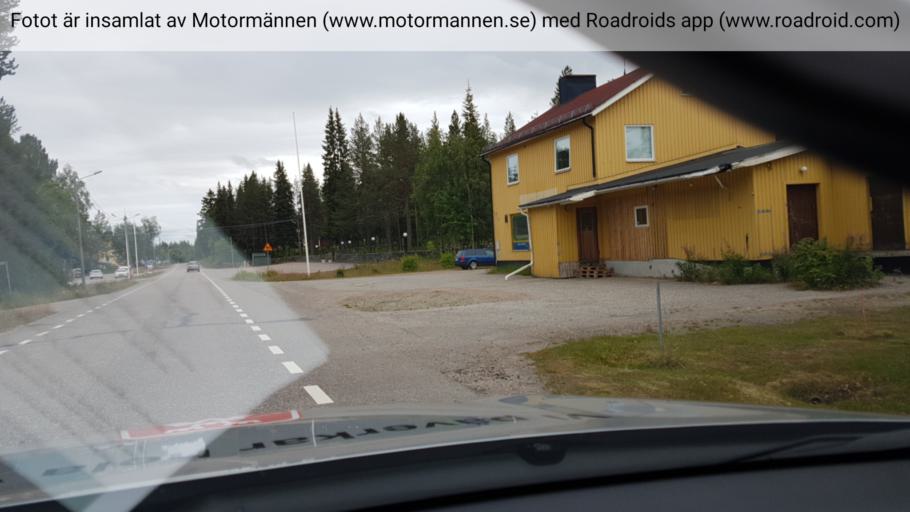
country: SE
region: Norrbotten
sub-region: Gallivare Kommun
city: Gaellivare
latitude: 67.0172
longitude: 21.8128
